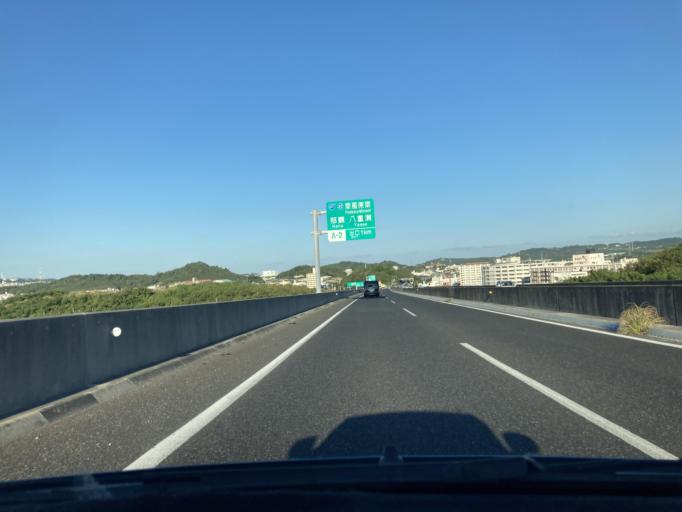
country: JP
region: Okinawa
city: Tomigusuku
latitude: 26.1771
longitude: 127.7097
